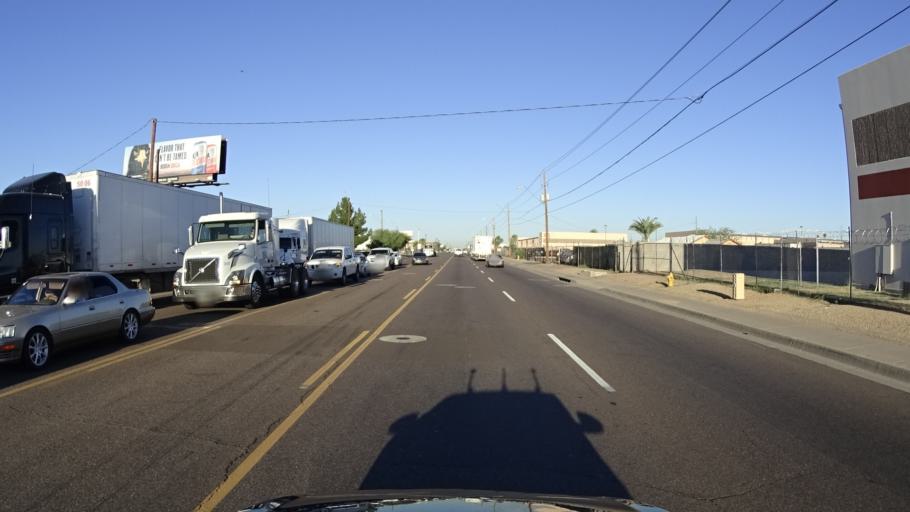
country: US
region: Arizona
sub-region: Maricopa County
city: Phoenix
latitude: 33.4369
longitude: -112.1395
